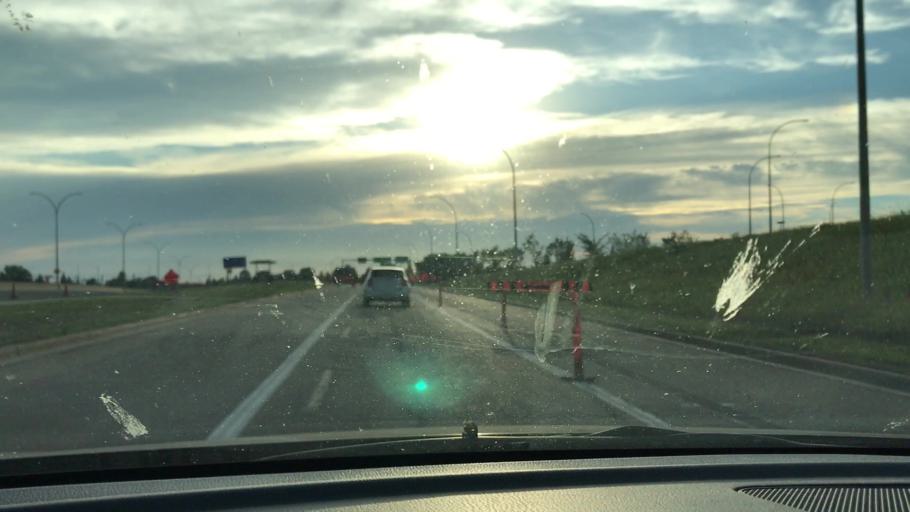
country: CA
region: Alberta
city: Edmonton
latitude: 53.4824
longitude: -113.5101
